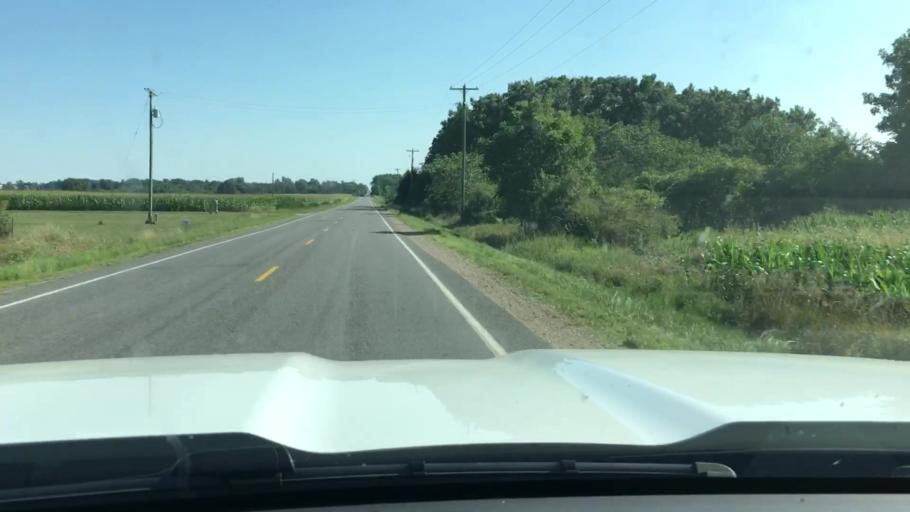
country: US
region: Michigan
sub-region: Muskegon County
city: Ravenna
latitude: 43.1554
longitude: -85.9278
